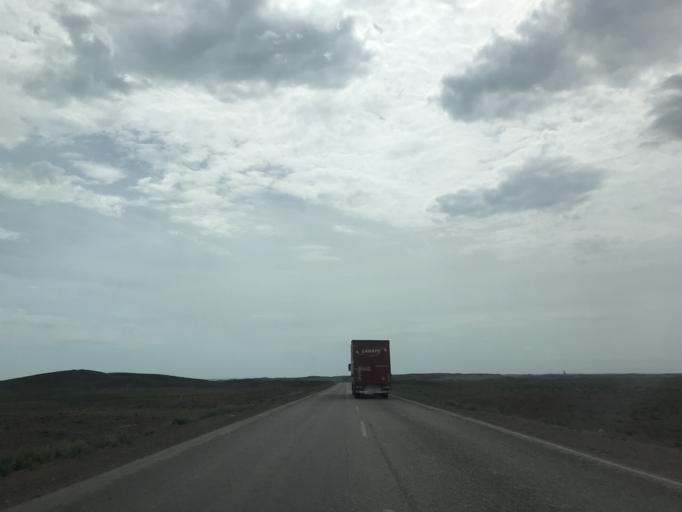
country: KZ
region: Zhambyl
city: Mynaral
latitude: 45.4647
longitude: 73.5710
